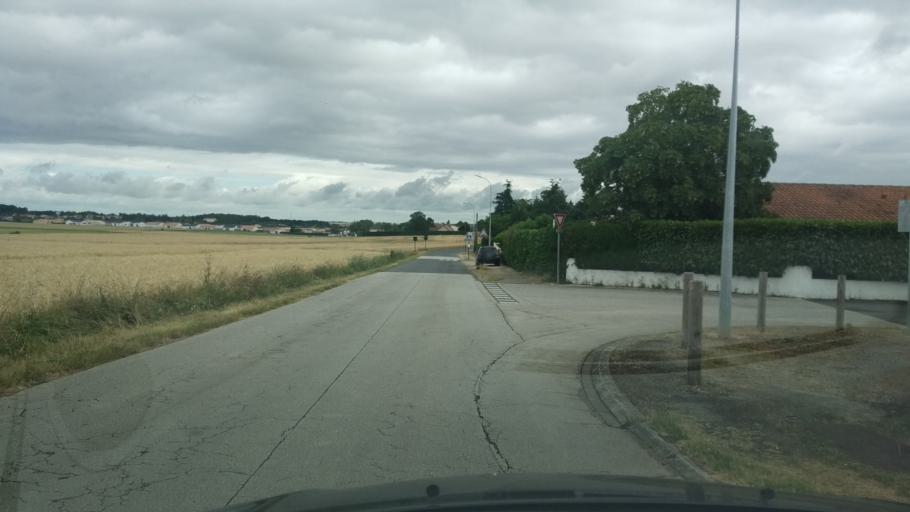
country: FR
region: Poitou-Charentes
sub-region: Departement de la Vienne
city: Vouneuil-sous-Biard
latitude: 46.5972
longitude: 0.2739
